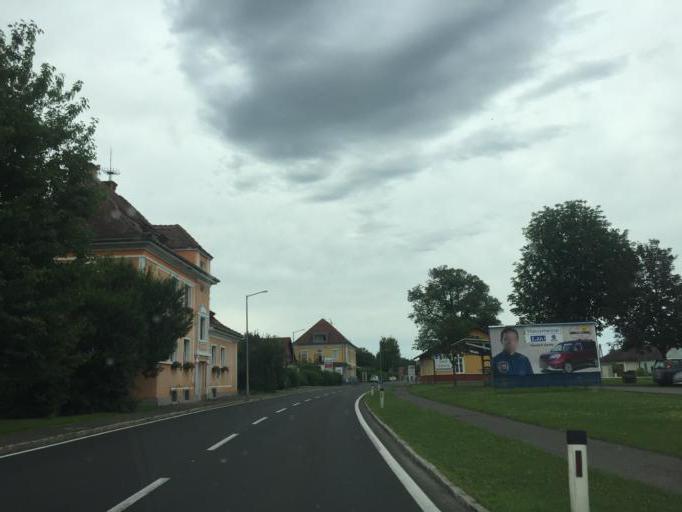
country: SI
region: Apace
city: Apace
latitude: 46.7319
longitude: 15.9024
